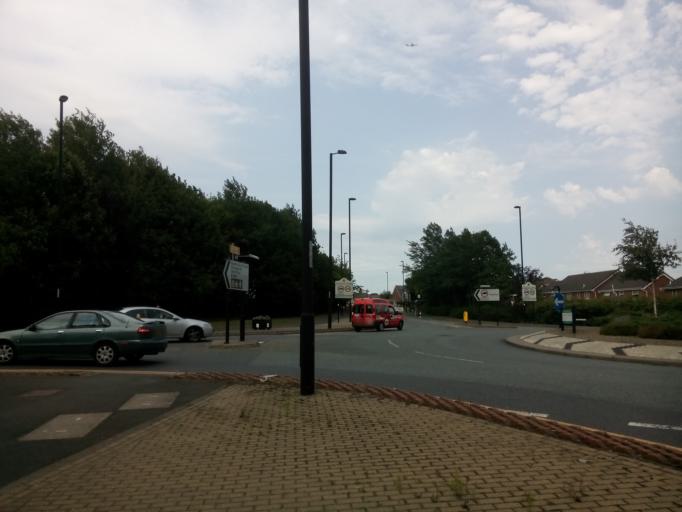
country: GB
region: England
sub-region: Northumberland
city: Backworth
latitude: 55.0233
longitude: -1.5346
